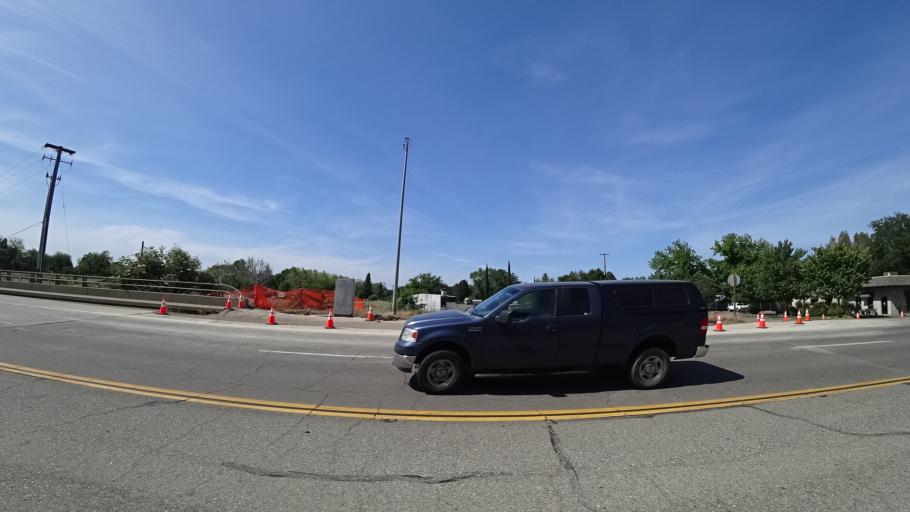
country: US
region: California
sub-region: Tehama County
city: Red Bluff
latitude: 40.1861
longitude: -122.2129
